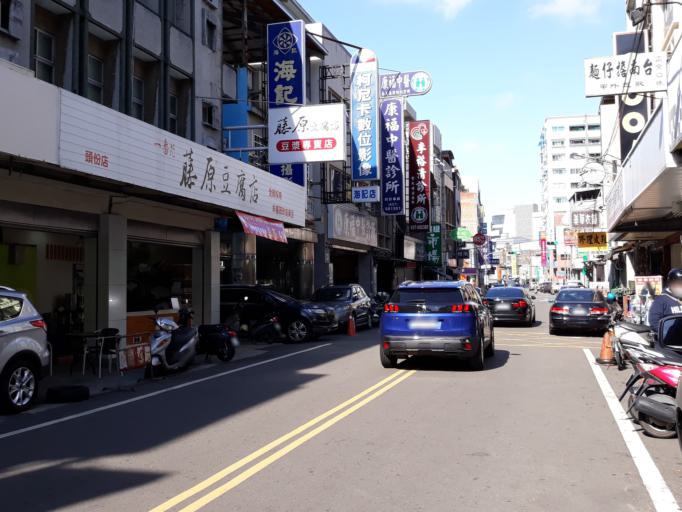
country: TW
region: Taiwan
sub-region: Hsinchu
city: Hsinchu
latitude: 24.6840
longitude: 120.9079
